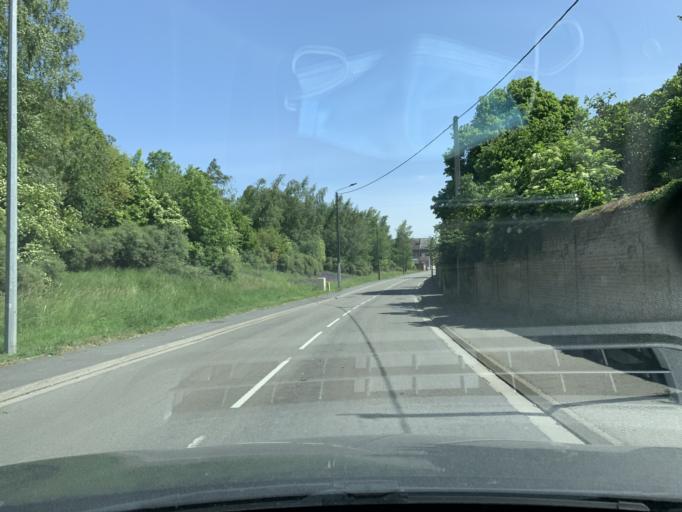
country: FR
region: Nord-Pas-de-Calais
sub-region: Departement du Nord
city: Masnieres
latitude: 50.1187
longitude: 3.2016
